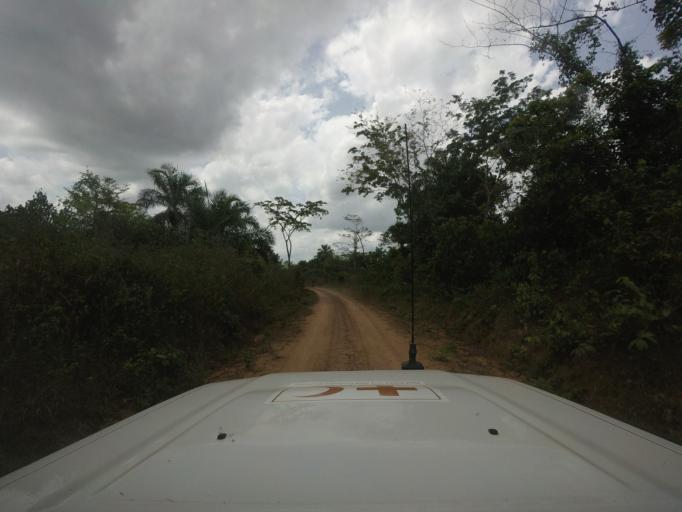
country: GN
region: Nzerekore
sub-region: Yomou
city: Yomou
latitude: 7.2748
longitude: -9.1861
